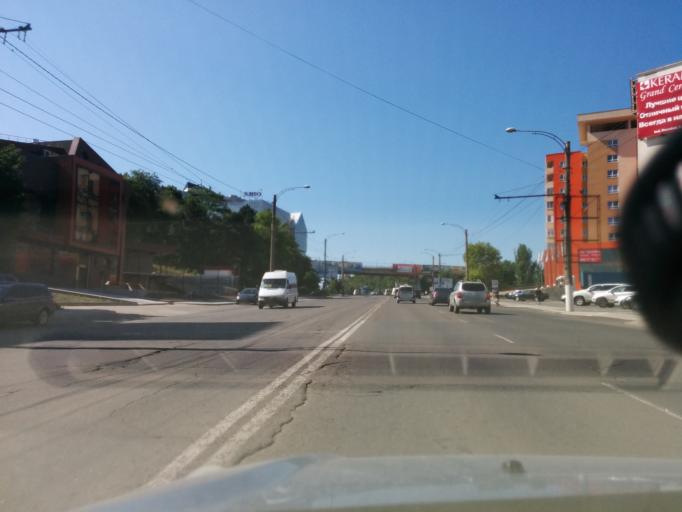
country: MD
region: Chisinau
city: Chisinau
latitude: 47.0066
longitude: 28.8599
